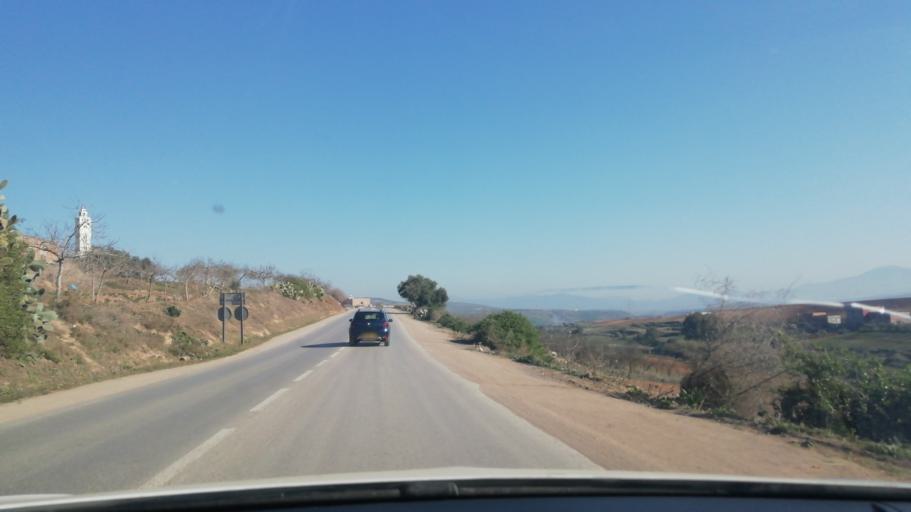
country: DZ
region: Tlemcen
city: Nedroma
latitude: 35.0049
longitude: -1.9028
